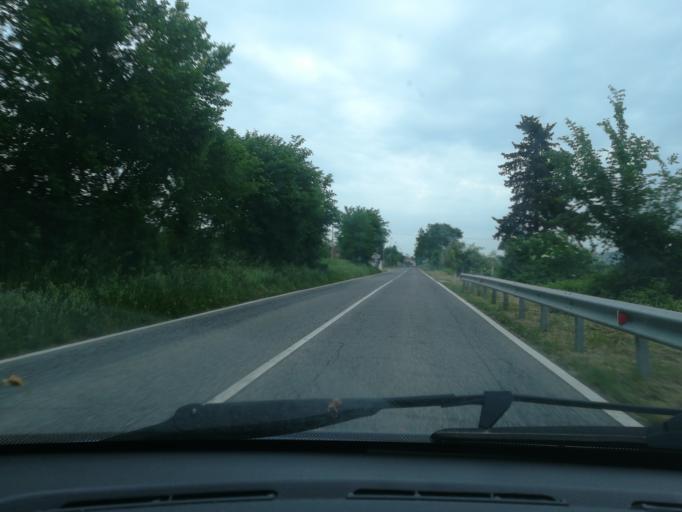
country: IT
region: The Marches
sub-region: Provincia di Macerata
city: Tolentino
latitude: 43.2663
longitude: 13.2569
